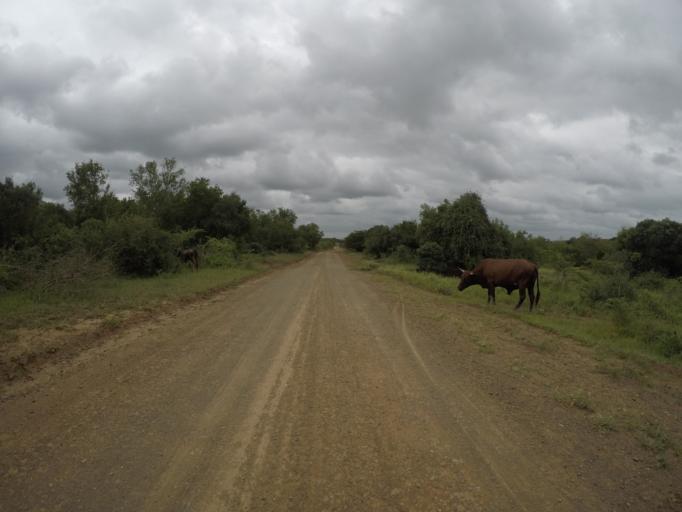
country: ZA
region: KwaZulu-Natal
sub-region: uThungulu District Municipality
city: Empangeni
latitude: -28.5587
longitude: 31.8777
